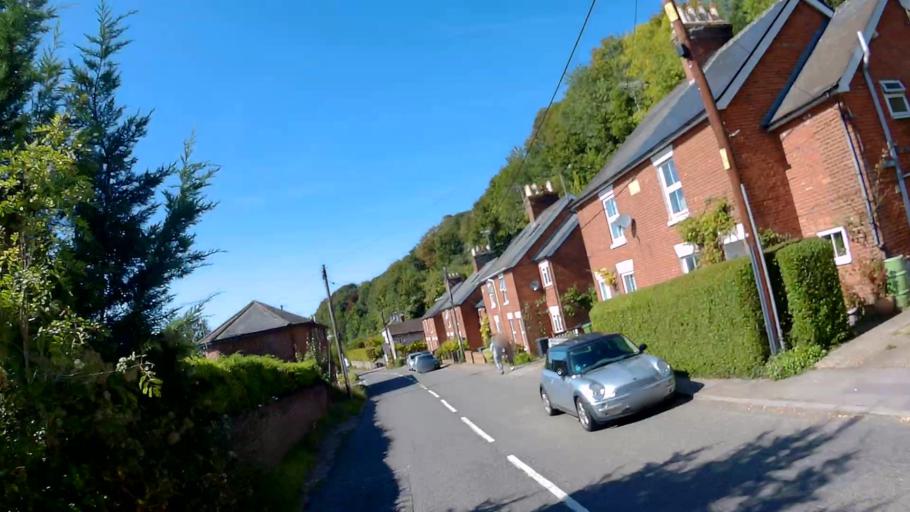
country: GB
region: England
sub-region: Hampshire
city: Overton
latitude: 51.2319
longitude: -1.3312
